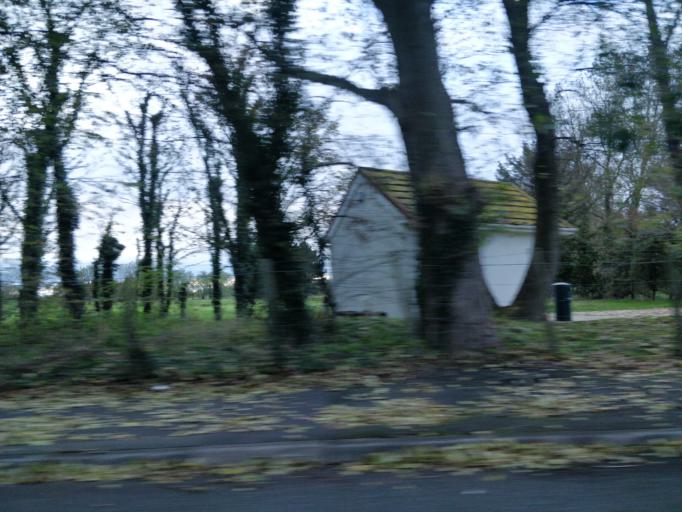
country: GB
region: England
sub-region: Sefton
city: Southport
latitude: 53.6647
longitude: -2.9820
